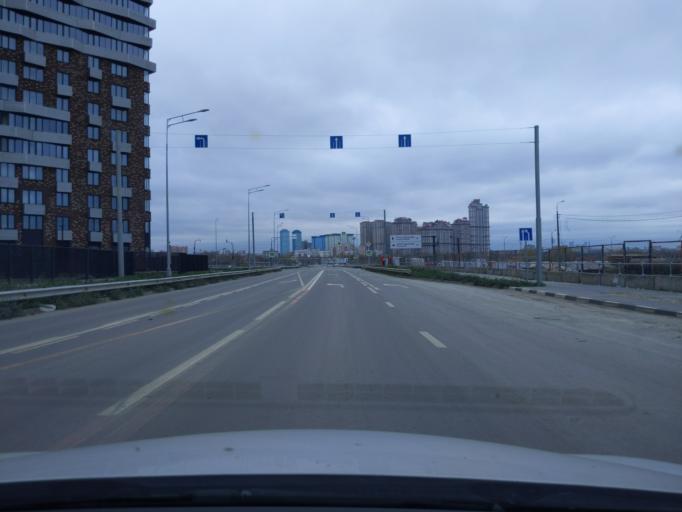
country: RU
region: Moscow
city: Strogino
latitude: 55.8156
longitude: 37.4294
